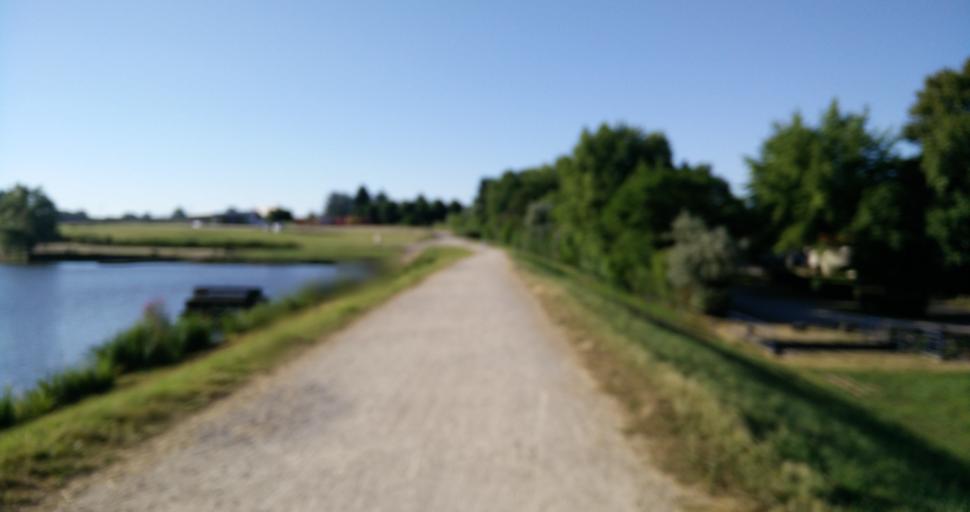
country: FR
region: Auvergne
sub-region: Departement de l'Allier
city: Yzeure
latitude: 46.5451
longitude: 3.3697
